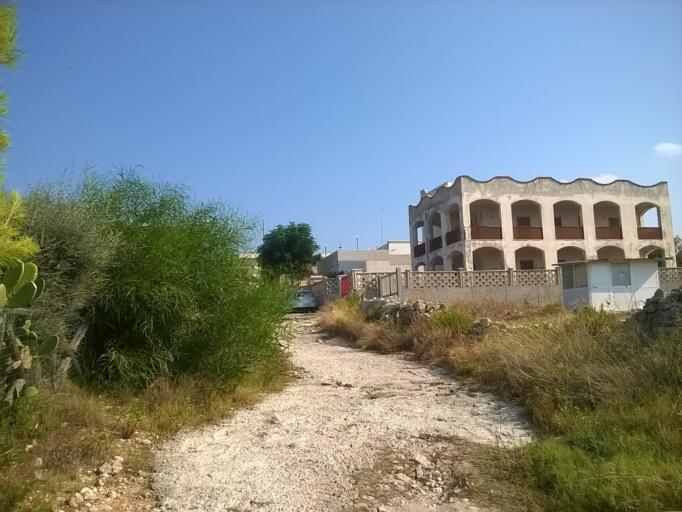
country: IT
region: Apulia
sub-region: Provincia di Taranto
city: Taranto
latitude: 40.3963
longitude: 17.2557
